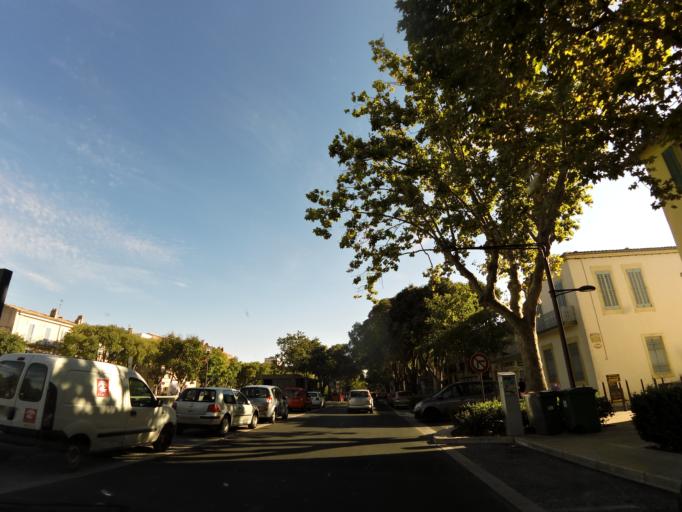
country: FR
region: Languedoc-Roussillon
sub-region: Departement du Gard
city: Nimes
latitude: 43.8358
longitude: 4.3506
